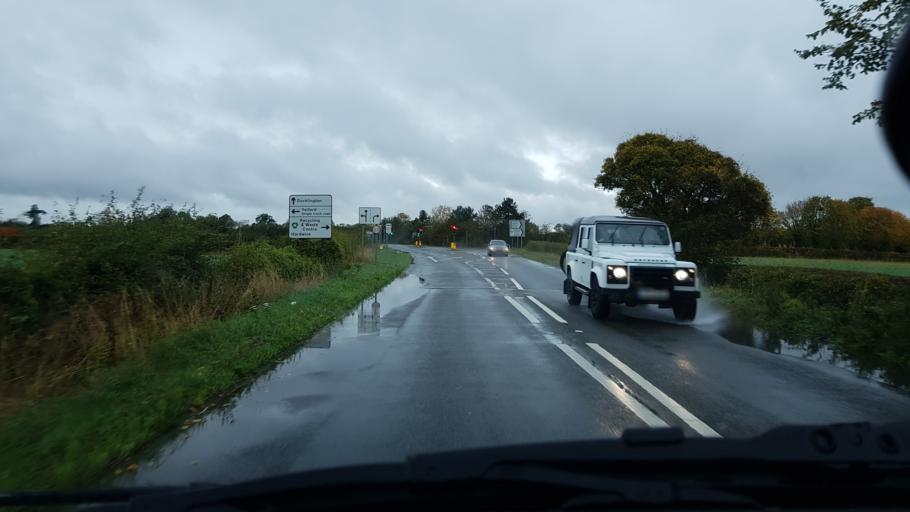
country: GB
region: England
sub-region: Oxfordshire
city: Ducklington
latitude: 51.7489
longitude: -1.4542
